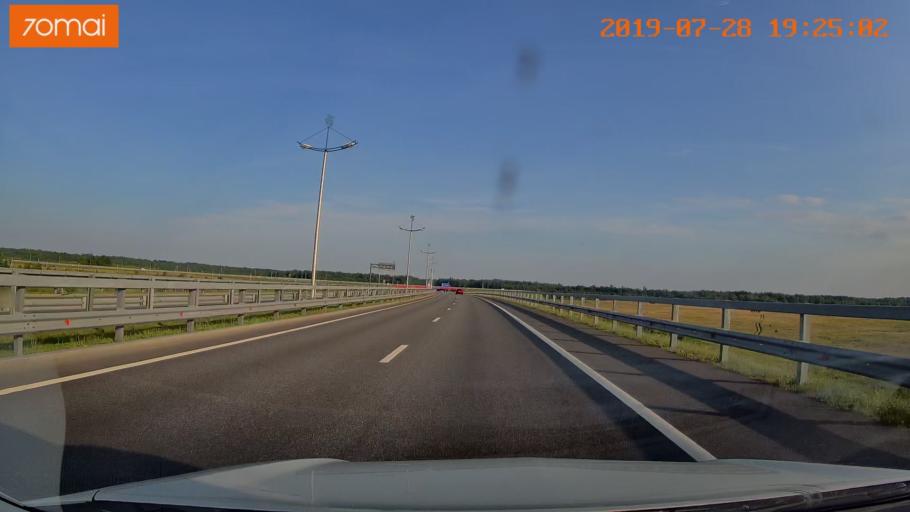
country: RU
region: Kaliningrad
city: Gur'yevsk
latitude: 54.8512
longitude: 20.5565
